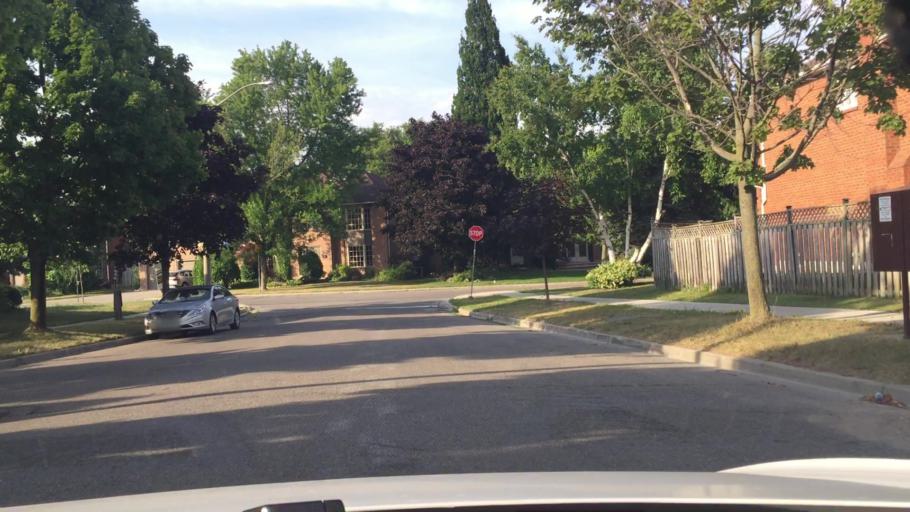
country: CA
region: Ontario
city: Pickering
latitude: 43.8014
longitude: -79.1503
